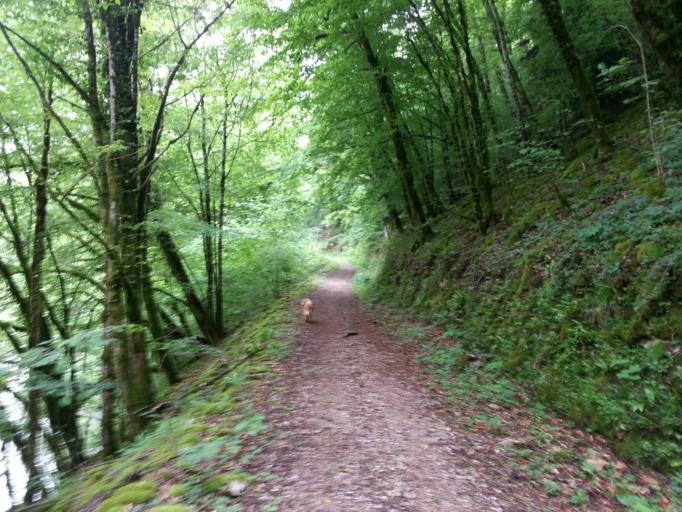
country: FR
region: Franche-Comte
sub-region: Departement du Doubs
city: Levier
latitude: 47.0020
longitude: 5.9981
